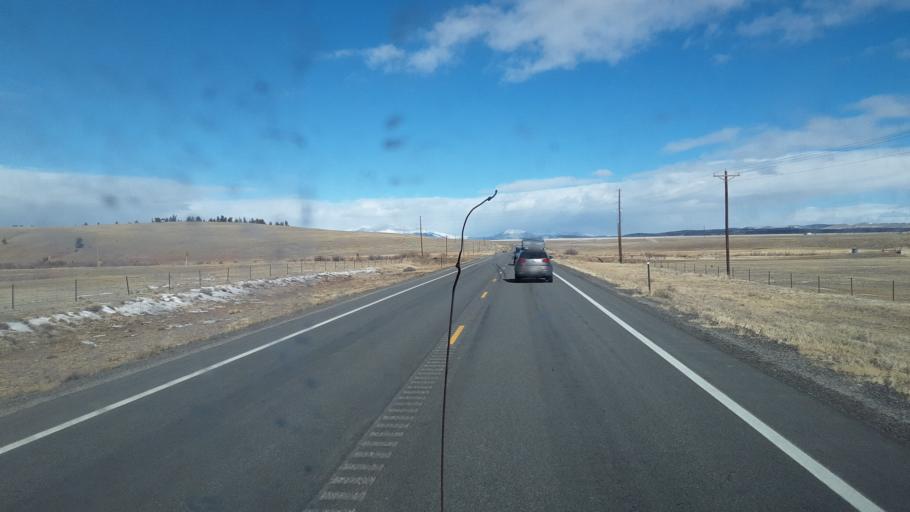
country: US
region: Colorado
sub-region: Park County
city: Fairplay
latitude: 39.0688
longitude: -105.9743
